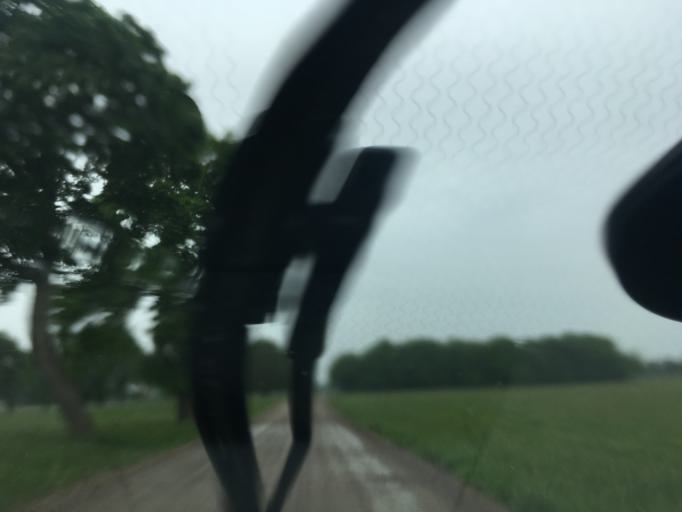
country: SE
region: Skane
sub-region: Lunds Kommun
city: Veberod
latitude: 55.6656
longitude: 13.4683
